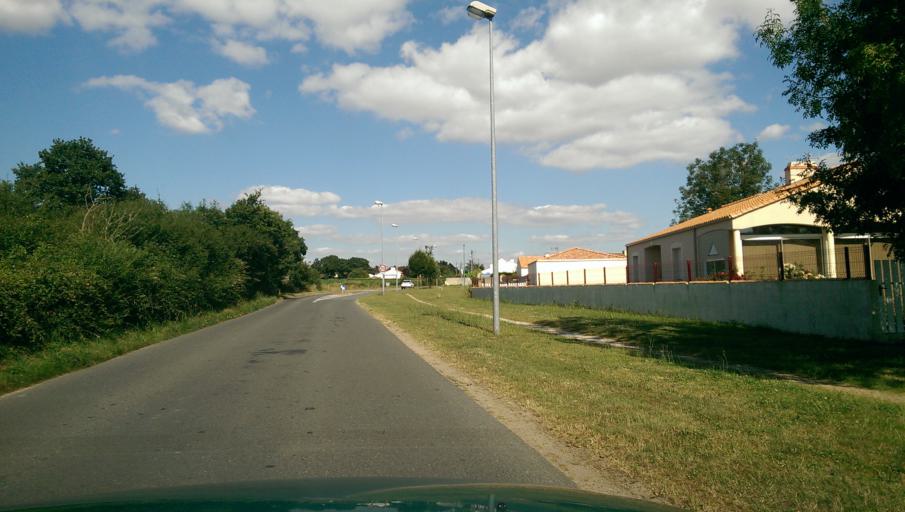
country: FR
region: Pays de la Loire
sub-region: Departement de la Loire-Atlantique
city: Lege
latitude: 46.8895
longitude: -1.5986
